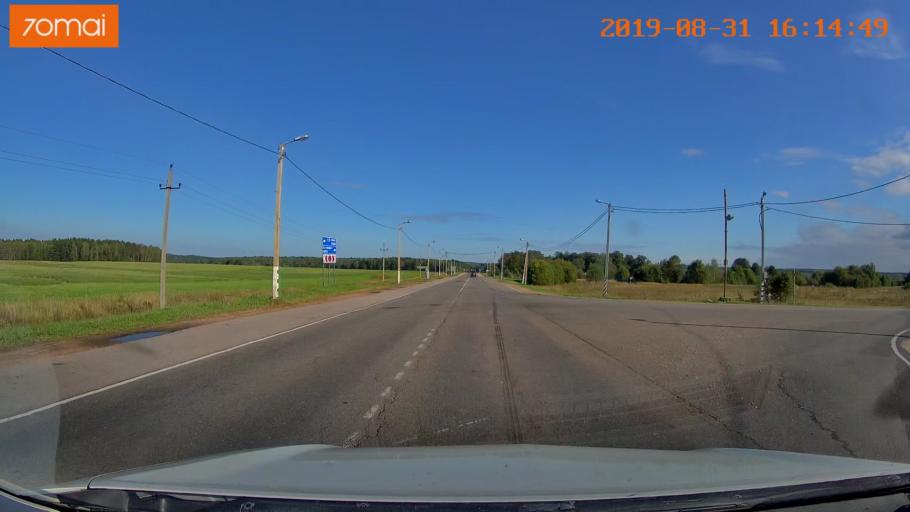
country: RU
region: Kaluga
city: Nikola-Lenivets
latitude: 54.5639
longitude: 35.4761
